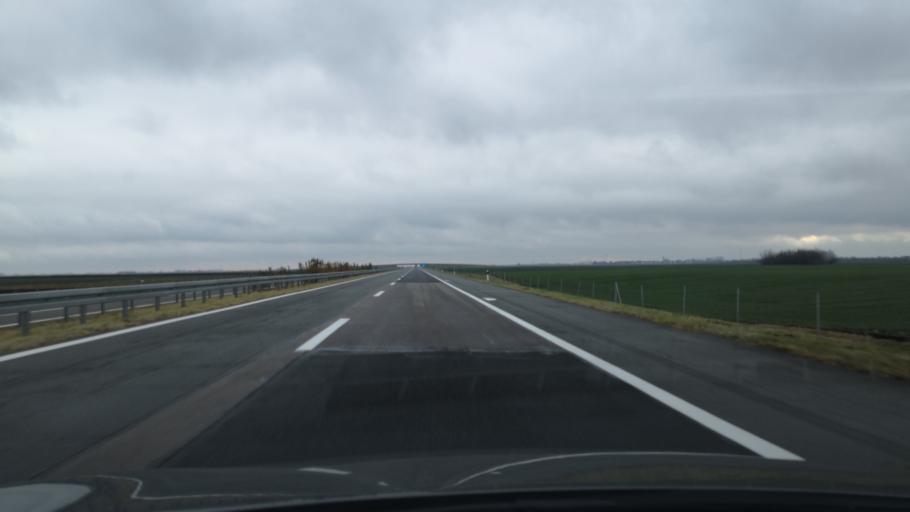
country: RS
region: Autonomna Pokrajina Vojvodina
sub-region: Severnobacki Okrug
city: Backa Topola
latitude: 45.8484
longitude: 19.6945
